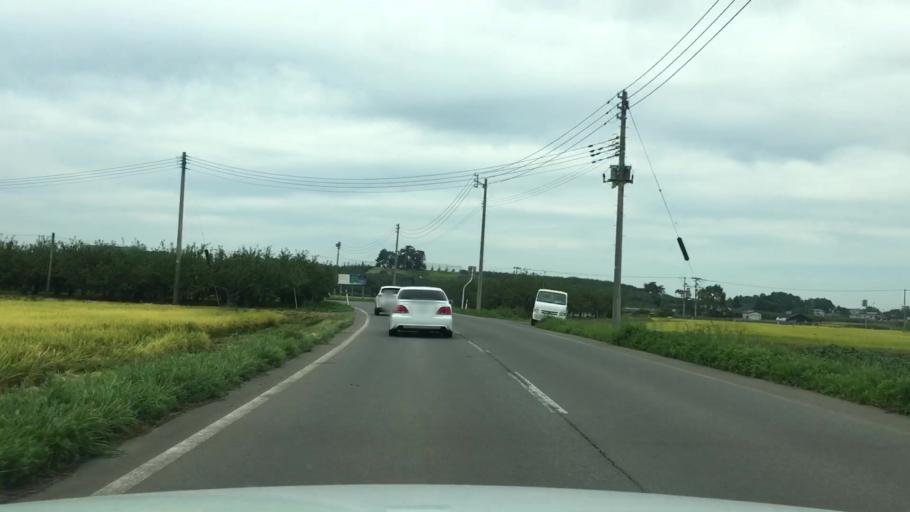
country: JP
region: Aomori
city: Hirosaki
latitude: 40.6579
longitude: 140.4195
